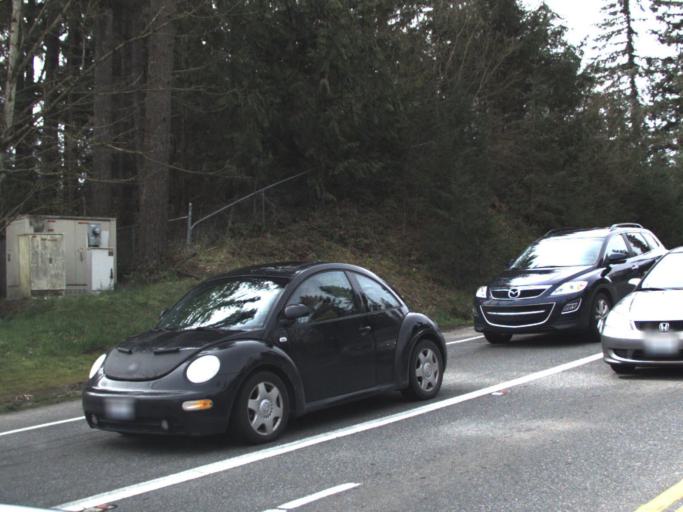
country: US
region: Washington
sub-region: King County
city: Maple Valley
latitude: 47.3580
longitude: -122.0442
